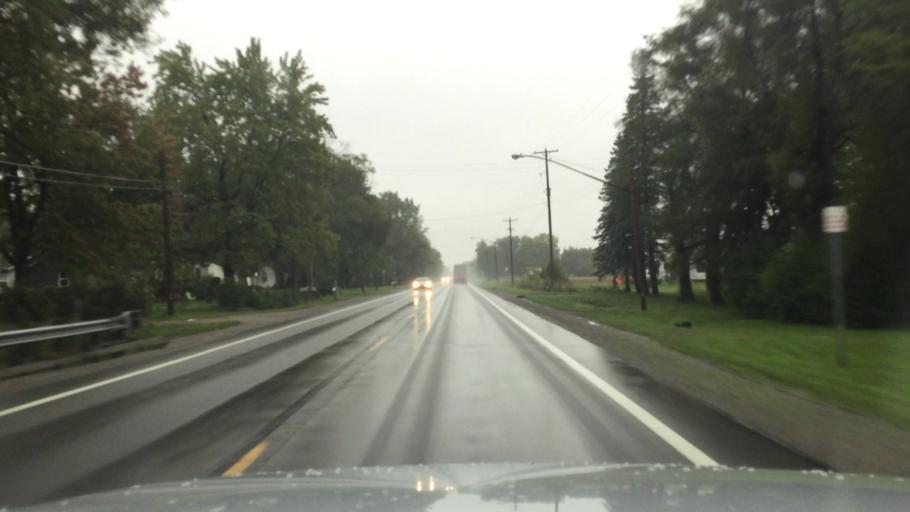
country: US
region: Michigan
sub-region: Saginaw County
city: Saginaw
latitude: 43.3846
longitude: -83.9554
